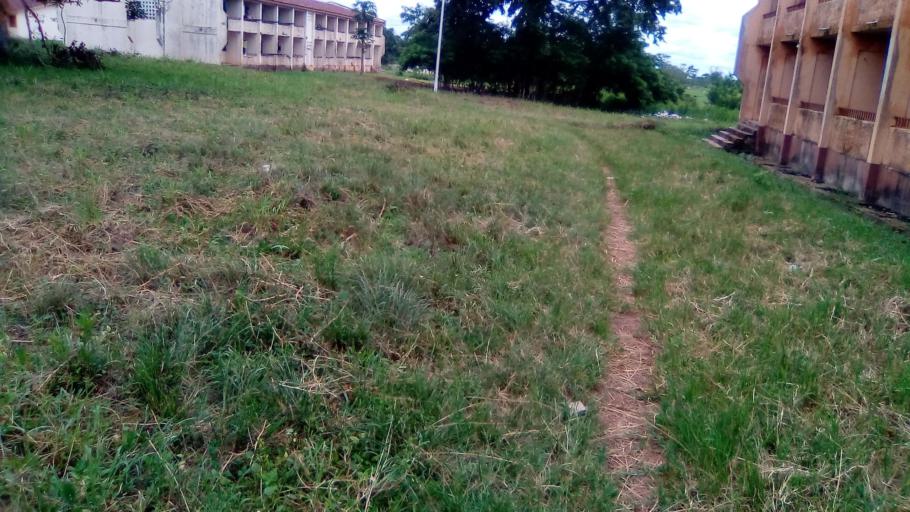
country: SL
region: Southern Province
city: Largo
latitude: 8.1191
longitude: -12.0699
